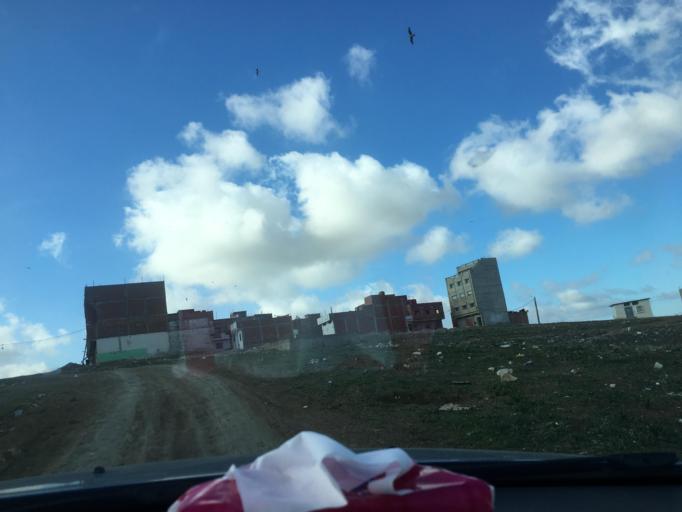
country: MA
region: Tanger-Tetouan
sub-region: Tanger-Assilah
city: Tangier
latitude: 35.7161
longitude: -5.8114
